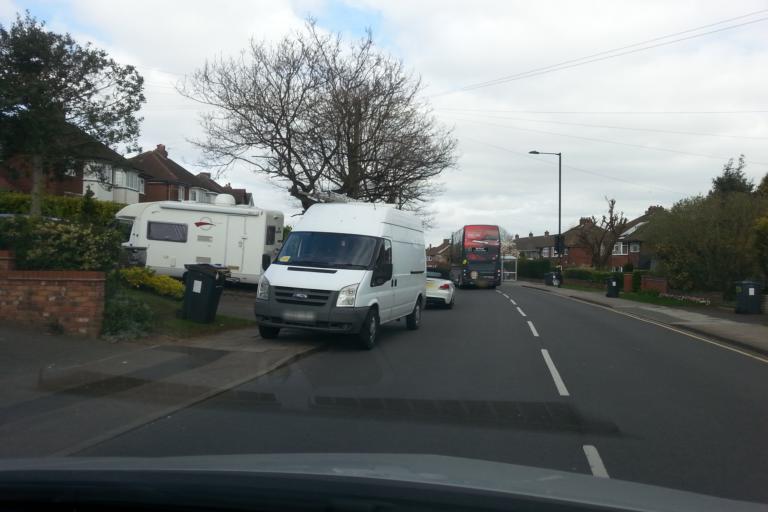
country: GB
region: England
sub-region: Staffordshire
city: Shenstone
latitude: 52.5957
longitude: -1.8443
